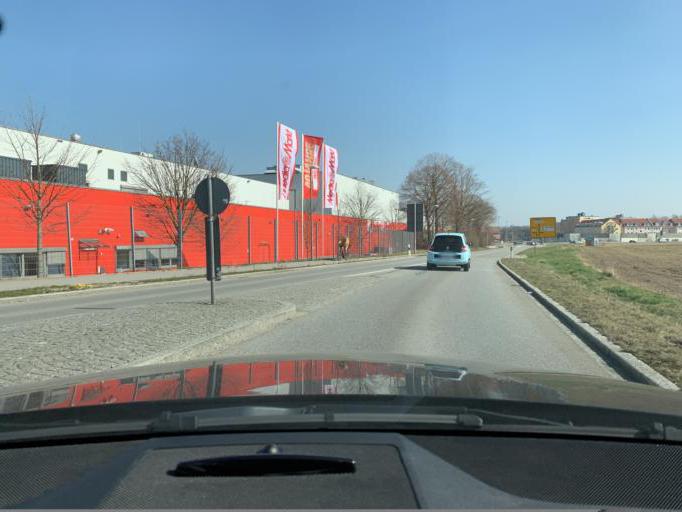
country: DE
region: Bavaria
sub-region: Upper Bavaria
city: Erding
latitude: 48.3057
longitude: 11.8886
